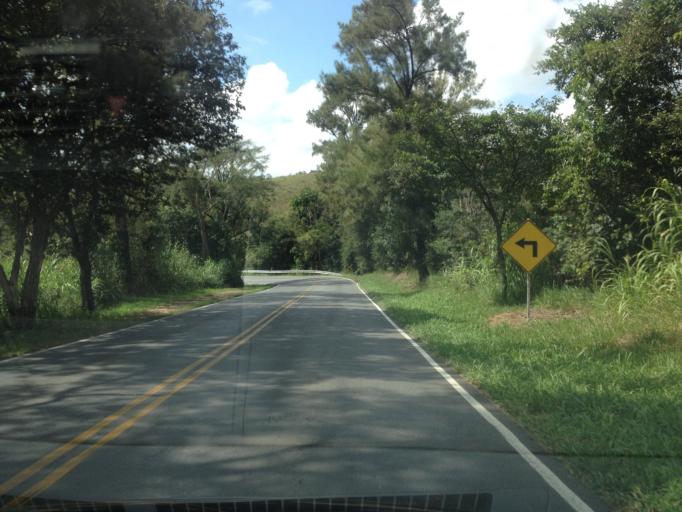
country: BR
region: Minas Gerais
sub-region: Itanhandu
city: Itanhandu
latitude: -22.2213
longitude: -44.9443
